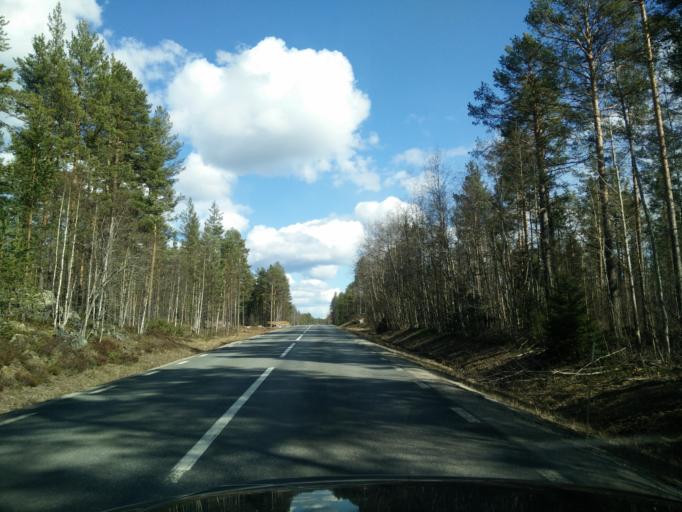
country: SE
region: Jaemtland
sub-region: Braecke Kommun
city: Braecke
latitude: 62.4515
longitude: 14.9316
